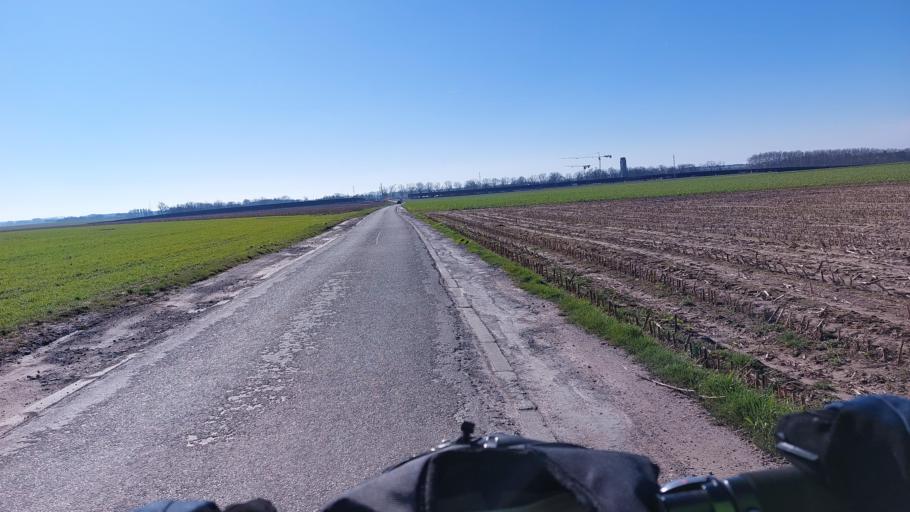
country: BE
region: Wallonia
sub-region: Province du Hainaut
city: Lens
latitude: 50.5960
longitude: 3.8949
